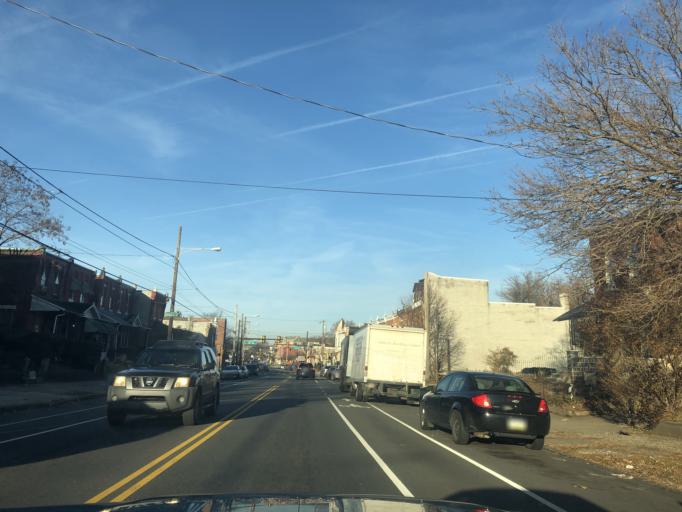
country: US
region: Pennsylvania
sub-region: Delaware County
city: Millbourne
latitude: 39.9665
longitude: -75.2286
